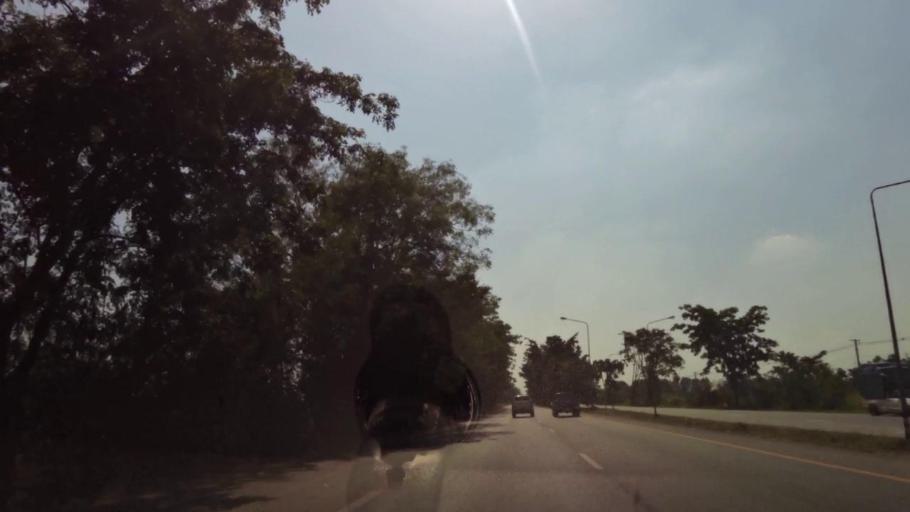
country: TH
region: Phichit
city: Wachira Barami
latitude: 16.4062
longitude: 100.1422
